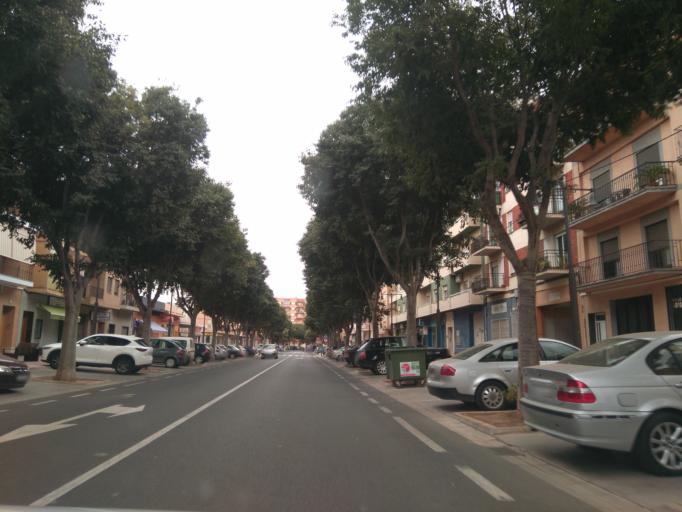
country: ES
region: Valencia
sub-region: Provincia de Valencia
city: L'Alcudia
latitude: 39.1970
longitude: -0.5035
